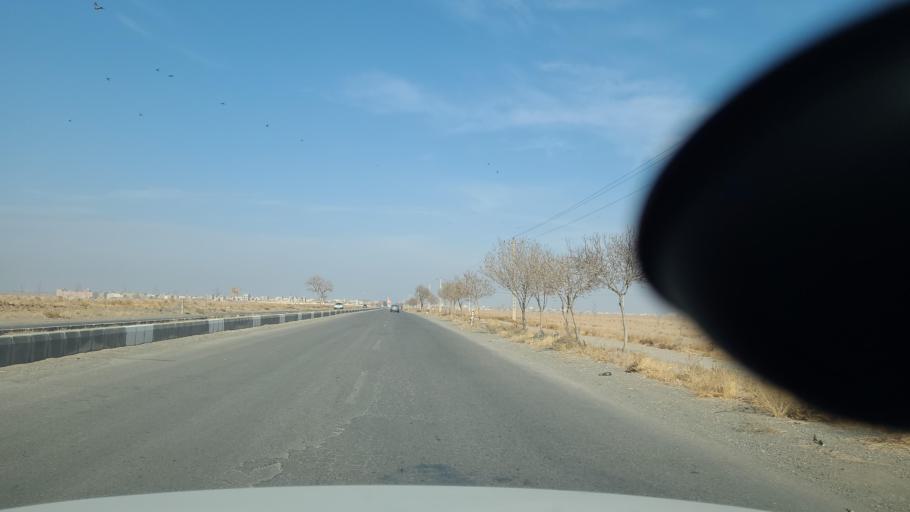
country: IR
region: Razavi Khorasan
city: Fariman
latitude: 35.6706
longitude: 59.8421
